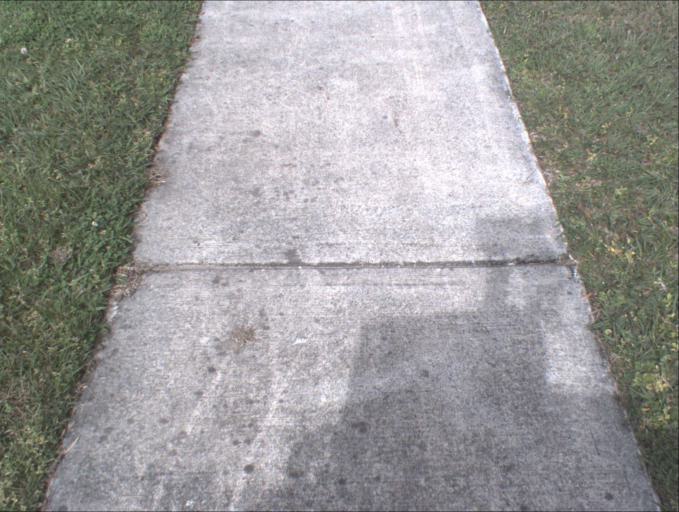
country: AU
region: Queensland
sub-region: Logan
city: Woodridge
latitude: -27.6559
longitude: 153.0659
